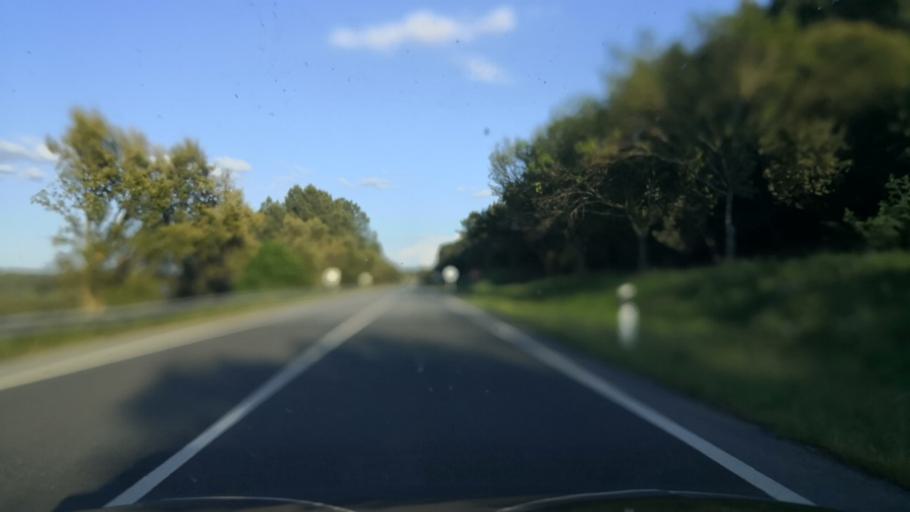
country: PT
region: Portalegre
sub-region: Marvao
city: Marvao
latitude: 39.3748
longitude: -7.3598
